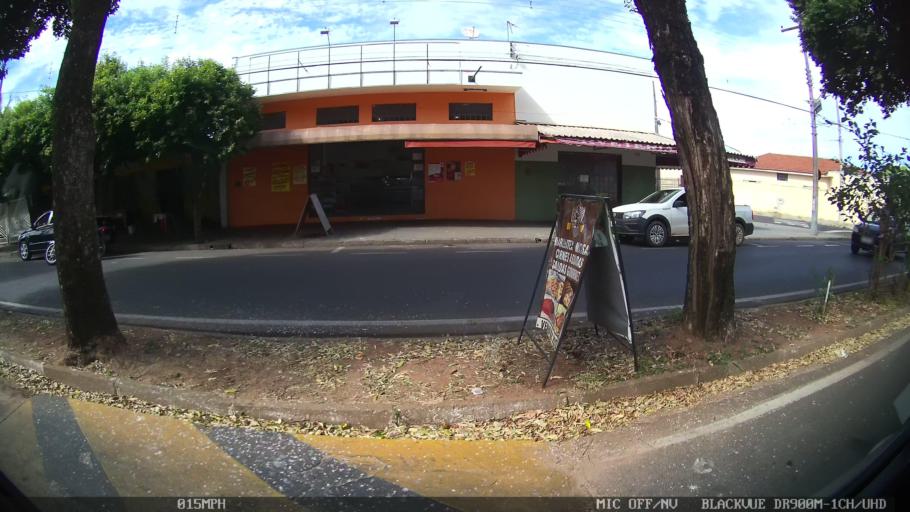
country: BR
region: Sao Paulo
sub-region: Catanduva
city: Catanduva
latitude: -21.1297
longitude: -48.9543
